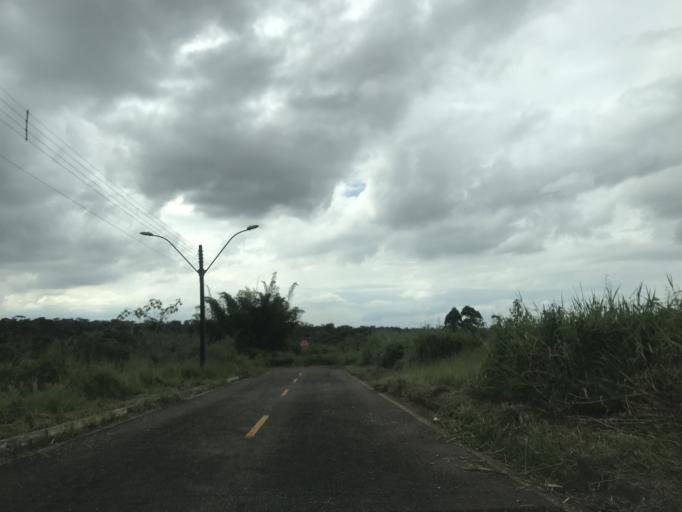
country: BR
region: Federal District
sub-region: Brasilia
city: Brasilia
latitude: -15.8910
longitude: -47.9307
